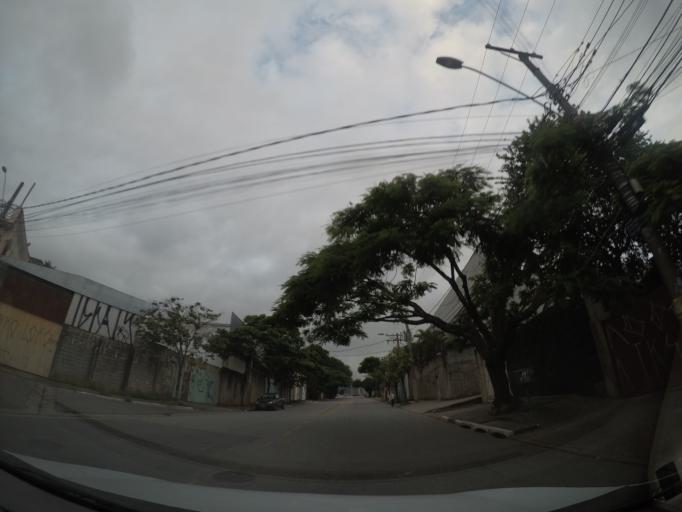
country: BR
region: Sao Paulo
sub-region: Aruja
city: Aruja
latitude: -23.4092
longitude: -46.4061
